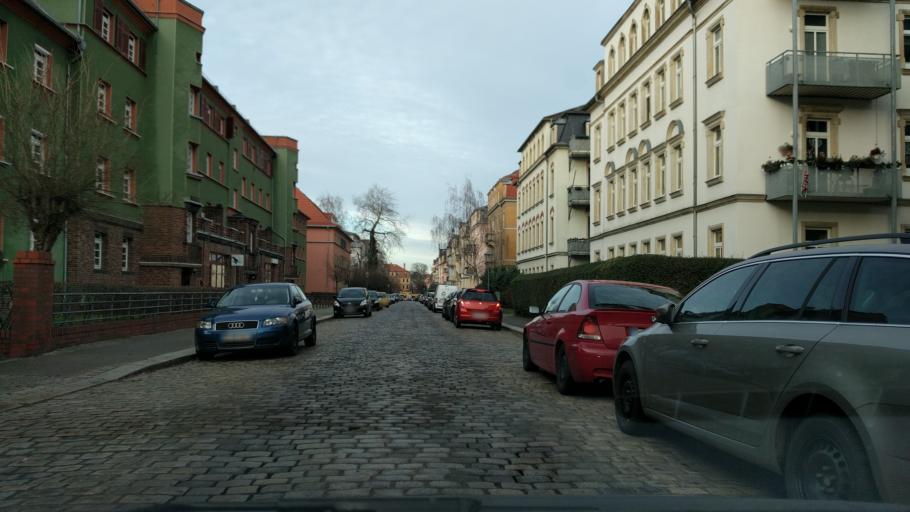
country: DE
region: Saxony
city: Dresden
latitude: 51.0398
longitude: 13.6929
